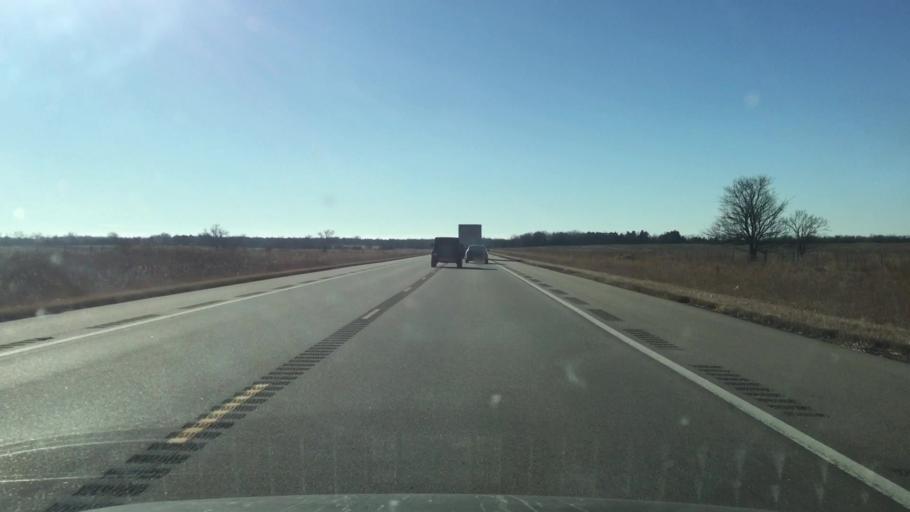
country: US
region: Kansas
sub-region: Allen County
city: Iola
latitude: 38.0464
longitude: -95.3805
